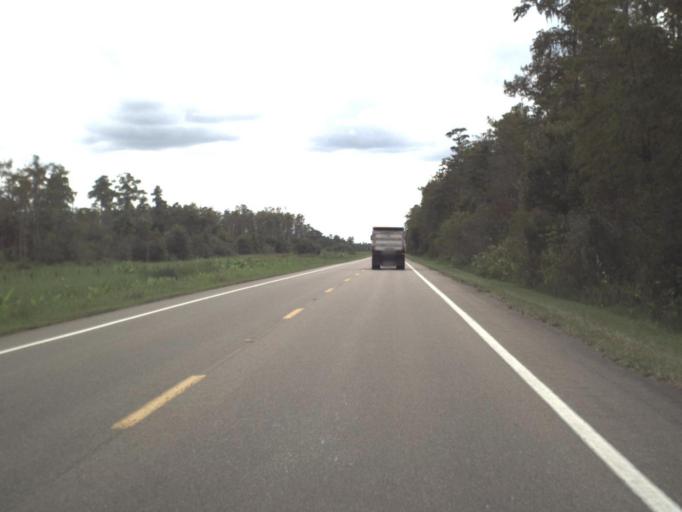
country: US
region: Florida
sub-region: Lee County
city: Olga
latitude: 26.9278
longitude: -81.7606
